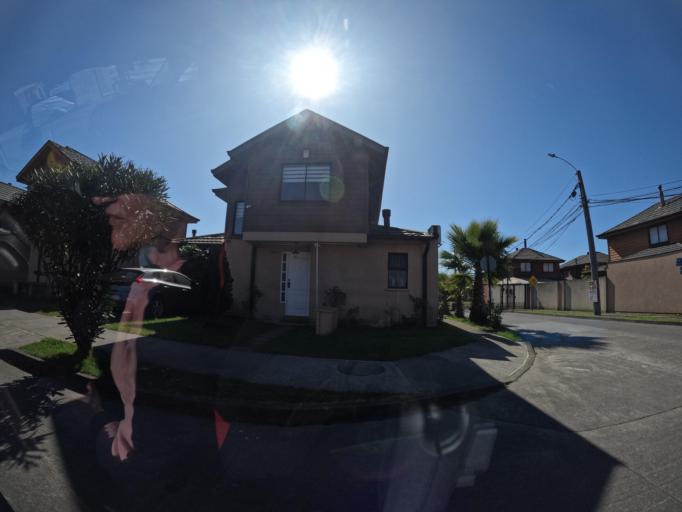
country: CL
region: Biobio
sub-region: Provincia de Concepcion
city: Concepcion
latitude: -36.8882
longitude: -73.1426
